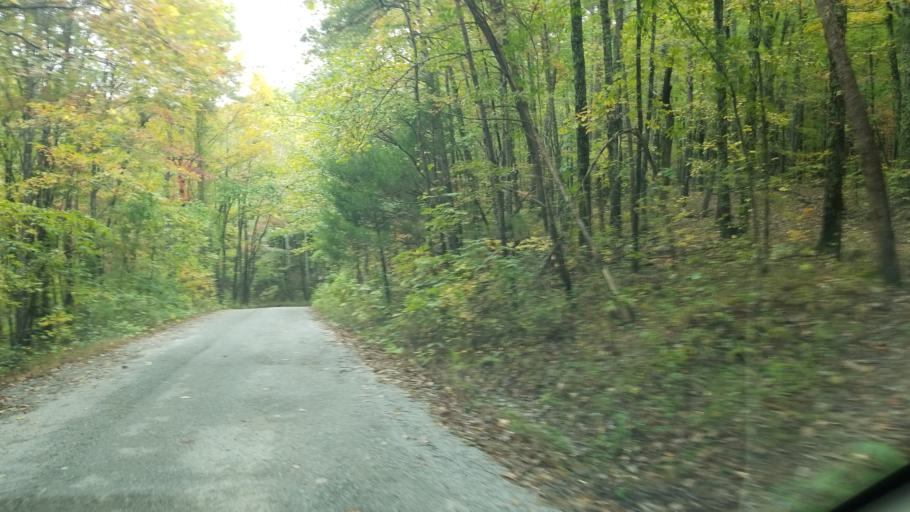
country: US
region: Tennessee
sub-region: Rhea County
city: Dayton
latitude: 35.5216
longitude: -85.0201
